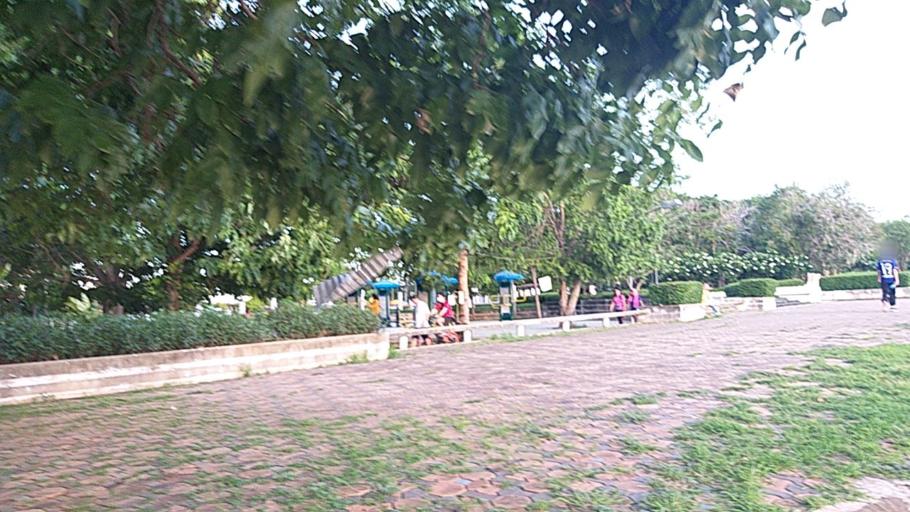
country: TH
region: Khon Kaen
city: Khon Kaen
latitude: 16.4132
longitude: 102.8406
